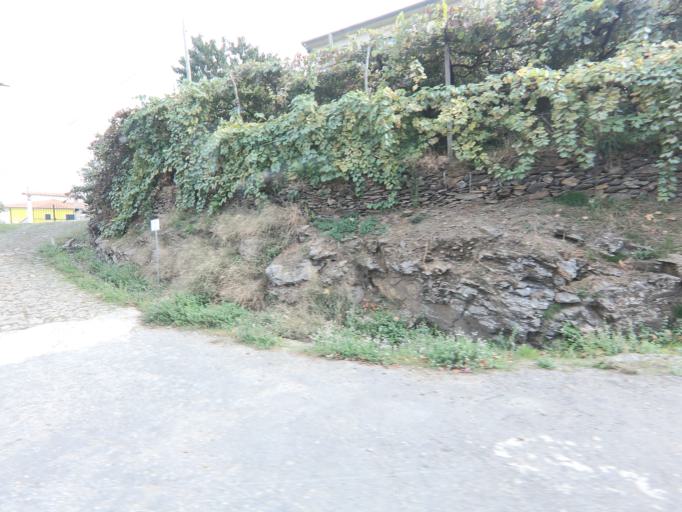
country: PT
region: Vila Real
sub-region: Mondim de Basto
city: Mondim de Basto
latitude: 41.3545
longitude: -7.8913
